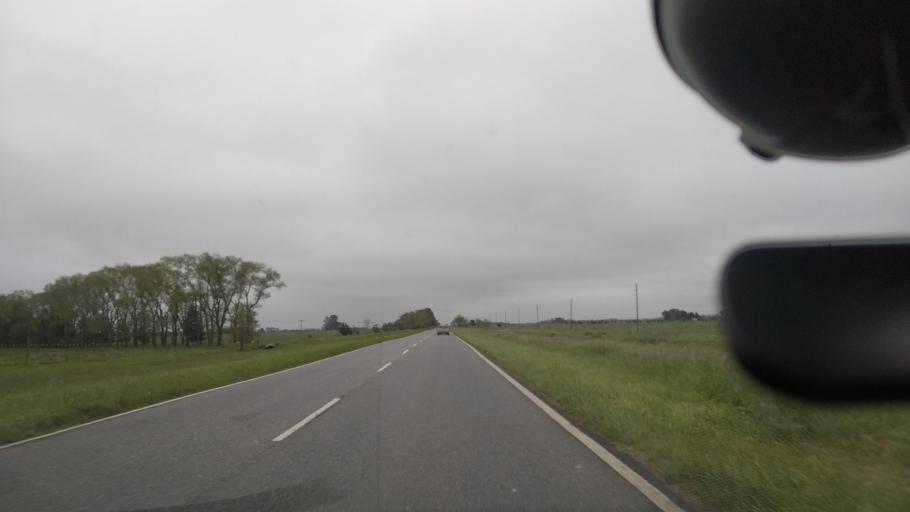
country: AR
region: Buenos Aires
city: Veronica
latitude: -35.3011
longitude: -57.5123
